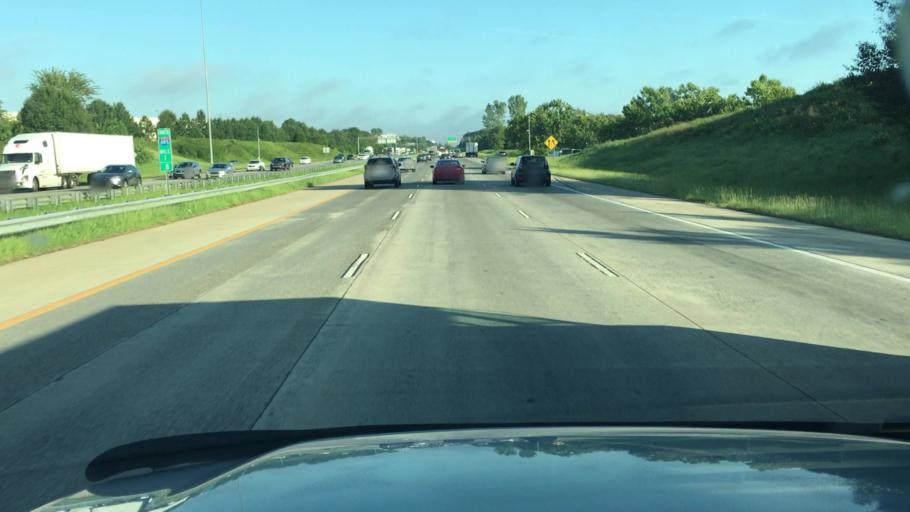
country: US
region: North Carolina
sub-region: Mecklenburg County
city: Pineville
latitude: 35.1426
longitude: -80.9330
